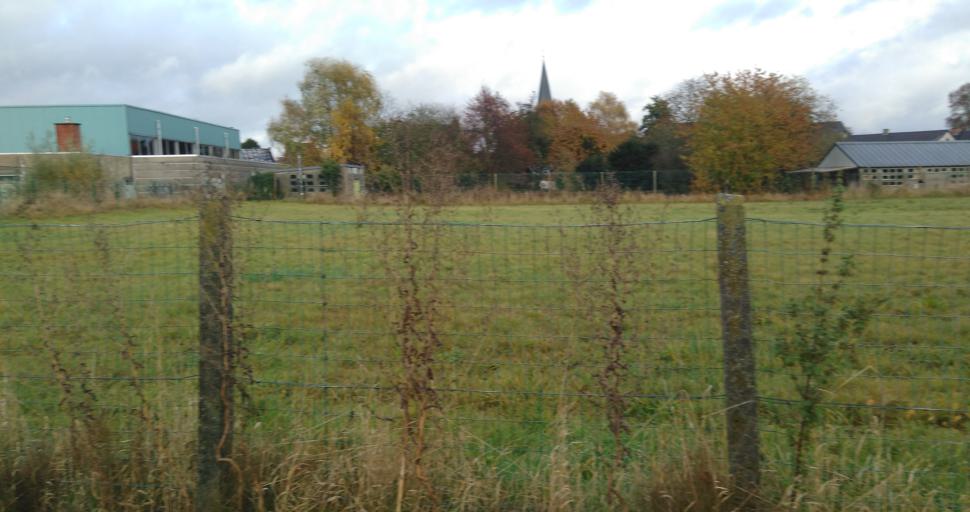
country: BE
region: Flanders
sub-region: Provincie Vlaams-Brabant
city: Herent
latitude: 50.8967
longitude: 4.6411
